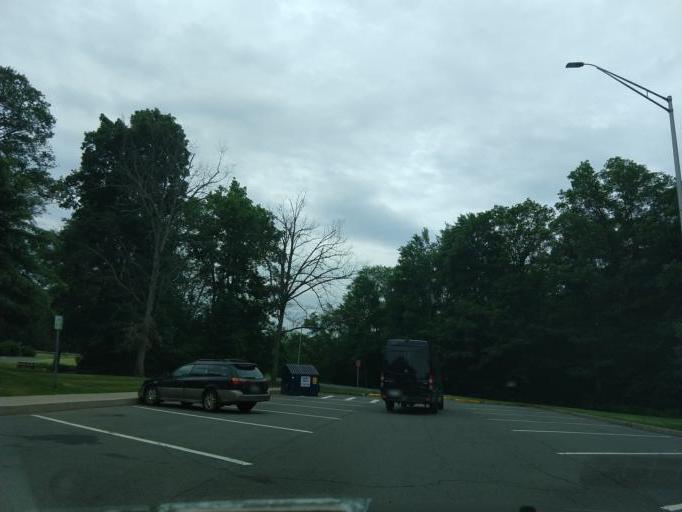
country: US
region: Pennsylvania
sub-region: Luzerne County
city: Nanticoke
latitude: 41.1305
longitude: -75.9642
